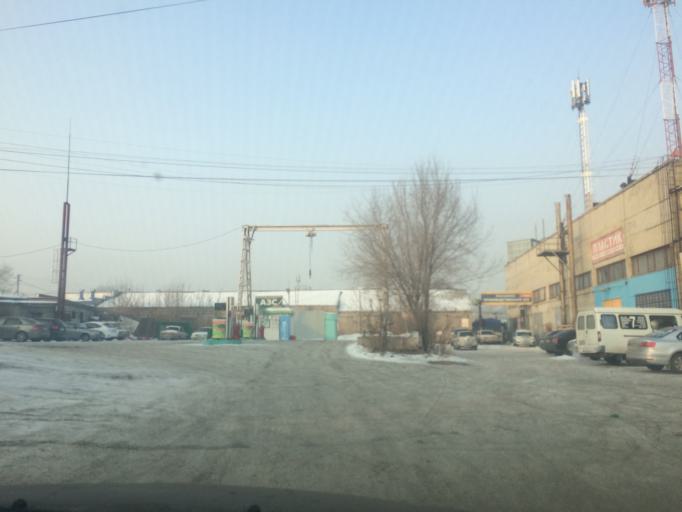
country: RU
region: Chelyabinsk
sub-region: Gorod Magnitogorsk
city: Magnitogorsk
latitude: 53.4203
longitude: 58.9627
